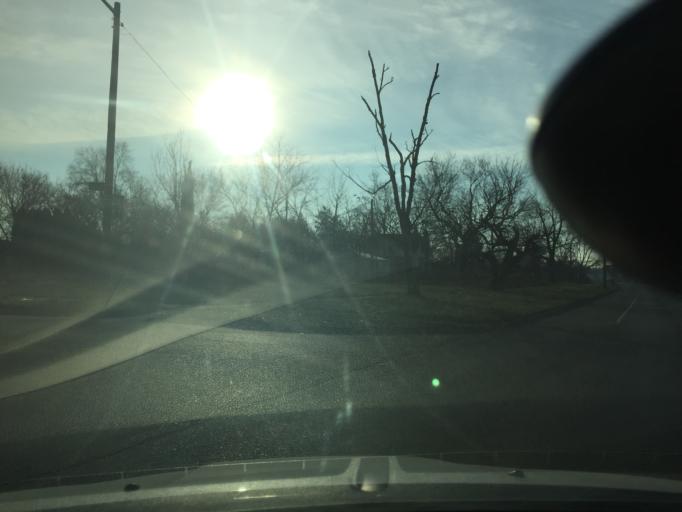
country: US
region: Michigan
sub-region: Macomb County
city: Eastpointe
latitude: 42.4382
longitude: -82.9655
